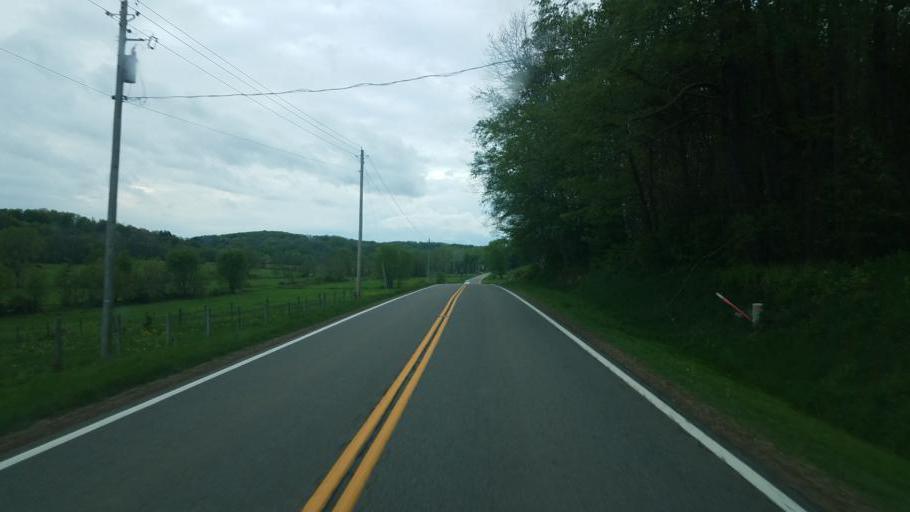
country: US
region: Ohio
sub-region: Sandusky County
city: Bellville
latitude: 40.5729
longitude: -82.4450
